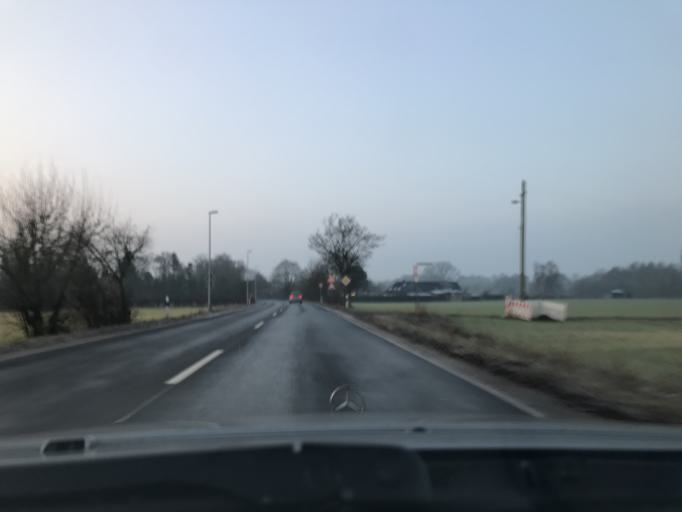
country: DE
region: North Rhine-Westphalia
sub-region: Regierungsbezirk Dusseldorf
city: Krefeld
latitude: 51.3929
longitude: 6.5990
